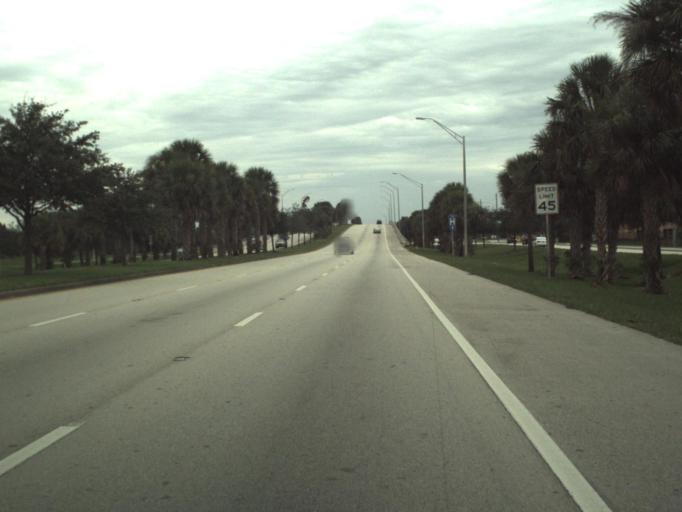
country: US
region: Florida
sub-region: Palm Beach County
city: Royal Palm Estates
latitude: 26.6783
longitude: -80.1159
